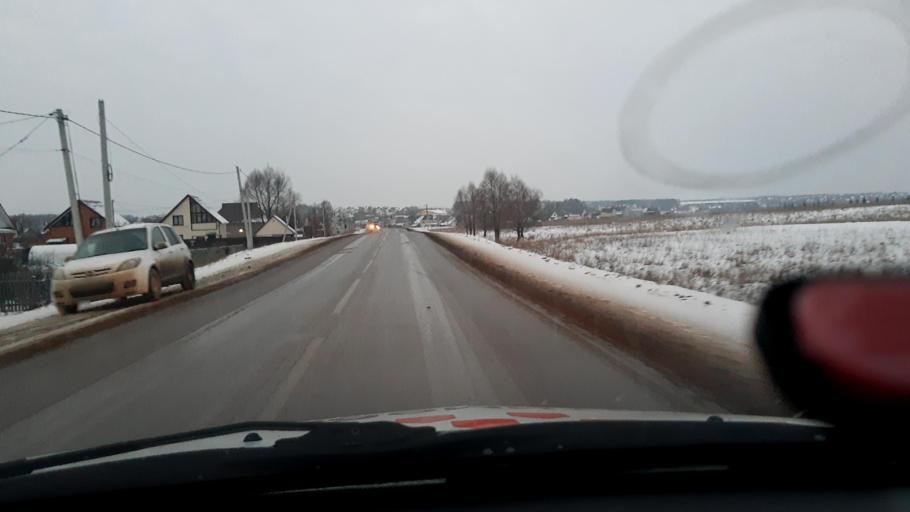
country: RU
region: Bashkortostan
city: Iglino
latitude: 54.8433
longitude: 56.4528
